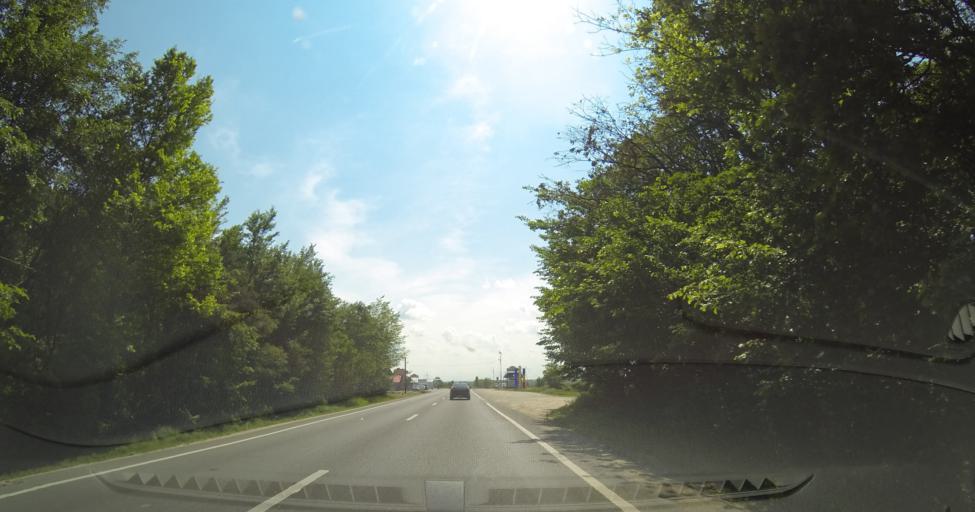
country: RO
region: Arges
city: Albota de Jos
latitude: 44.7354
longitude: 24.8044
